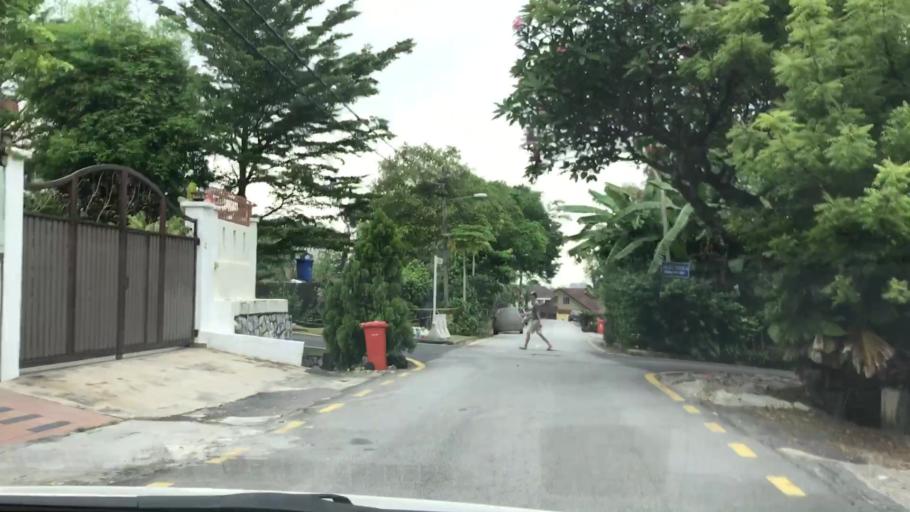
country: MY
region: Selangor
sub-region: Petaling
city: Petaling Jaya
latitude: 3.1090
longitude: 101.6204
